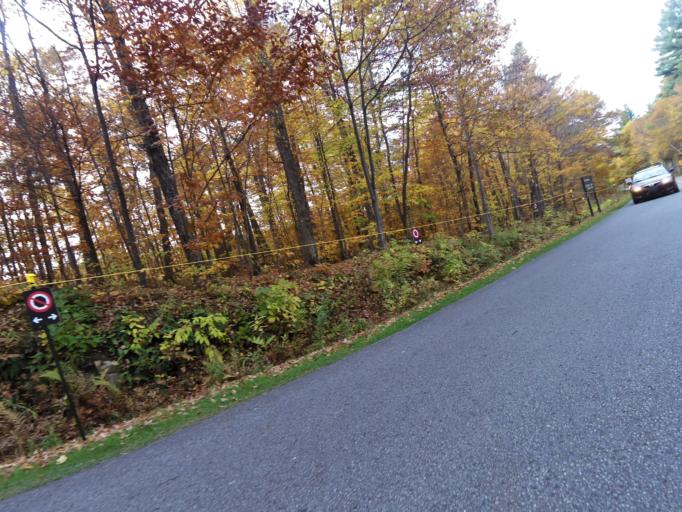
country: CA
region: Quebec
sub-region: Outaouais
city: Gatineau
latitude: 45.4779
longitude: -75.8461
